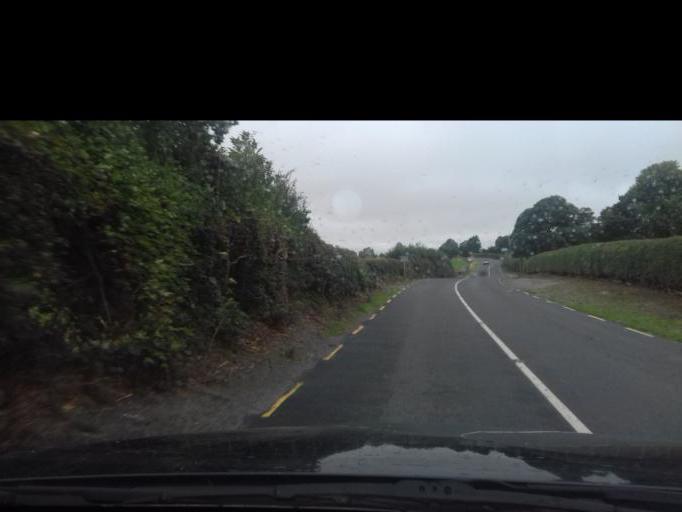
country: IE
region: Leinster
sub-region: County Carlow
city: Bagenalstown
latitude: 52.6360
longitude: -6.9419
